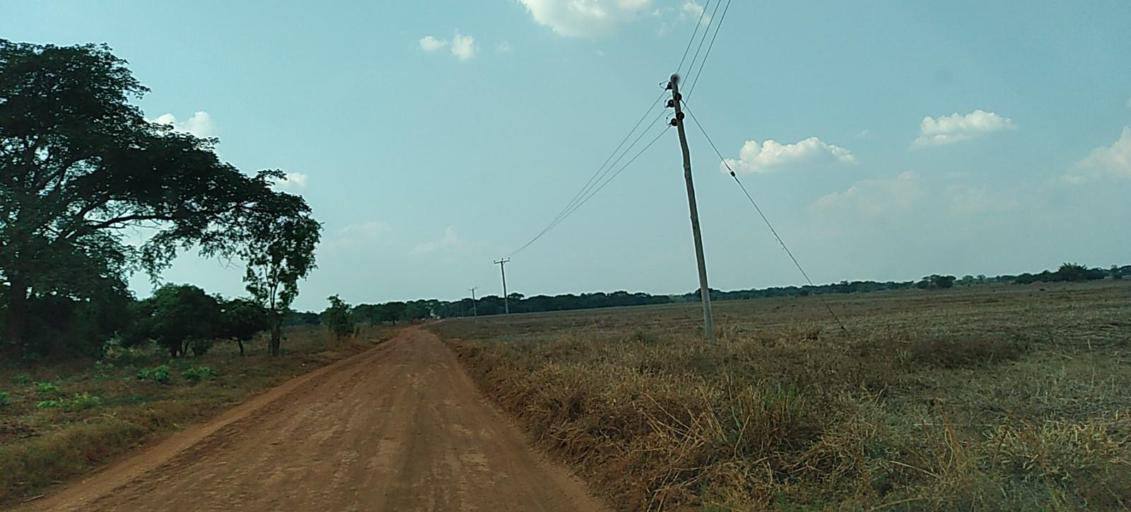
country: ZM
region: Copperbelt
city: Mpongwe
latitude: -13.5209
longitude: 28.0990
